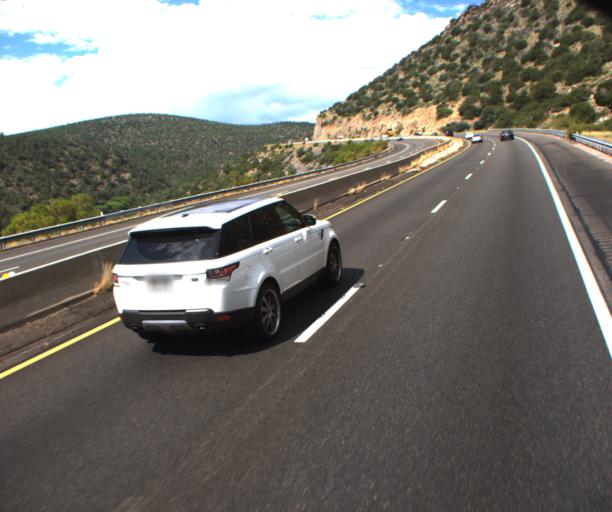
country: US
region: Arizona
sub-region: Yavapai County
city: Camp Verde
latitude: 34.5349
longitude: -111.9363
